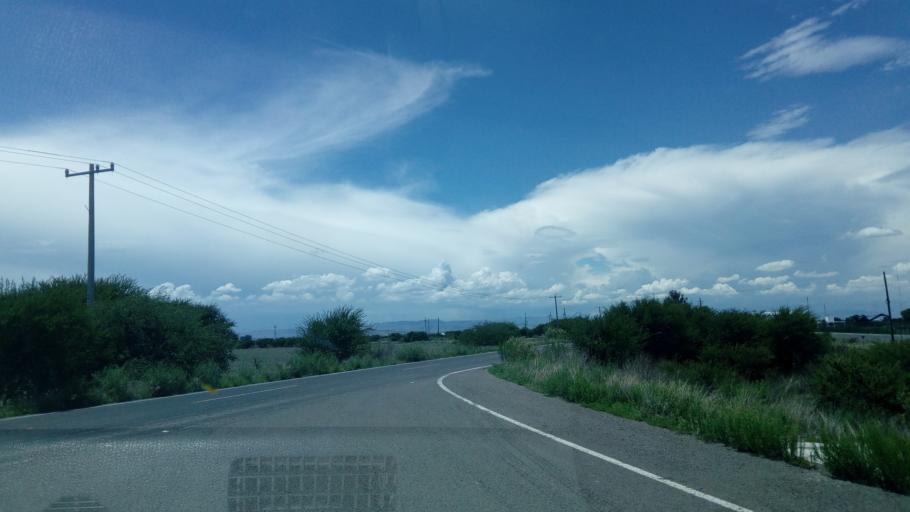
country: MX
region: Durango
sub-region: Durango
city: Jose Refugio Salcido
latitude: 24.1582
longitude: -104.5184
